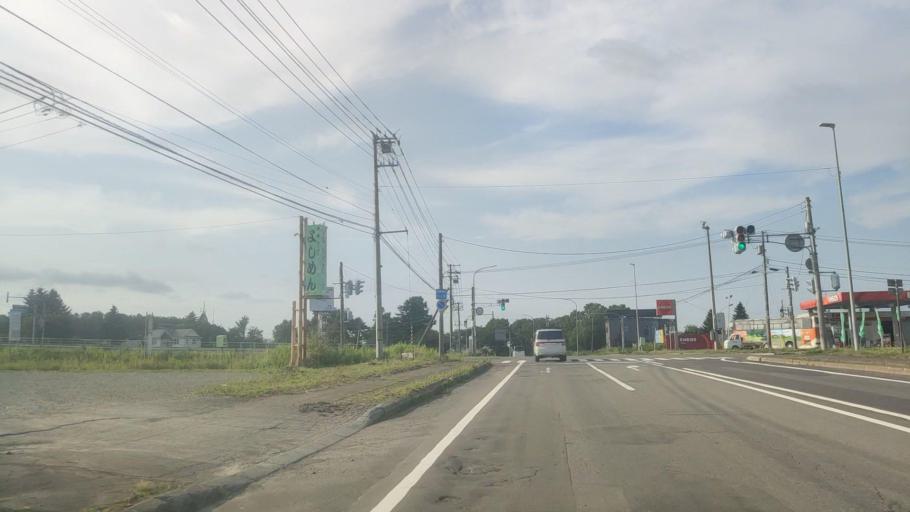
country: JP
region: Hokkaido
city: Chitose
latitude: 42.9498
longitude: 141.8026
